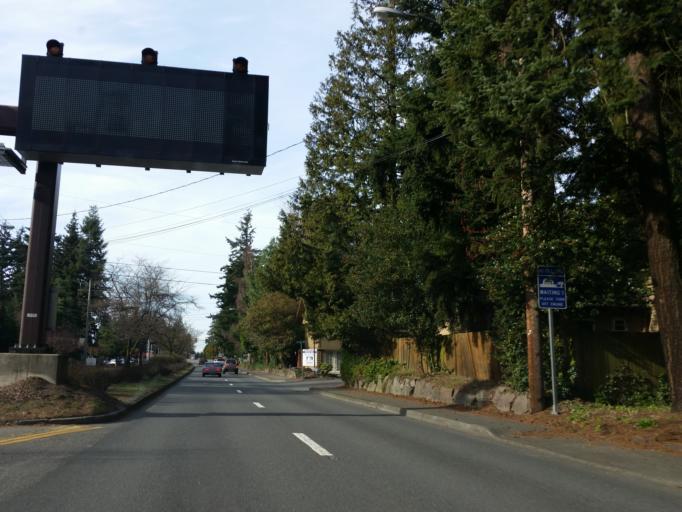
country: US
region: Washington
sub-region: Snohomish County
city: Woodway
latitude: 47.7927
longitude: -122.3702
